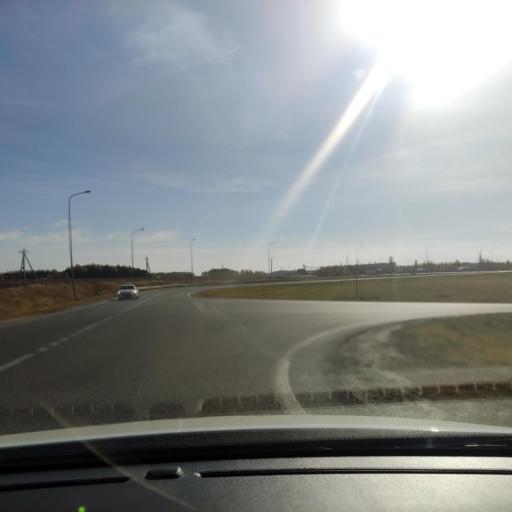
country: RU
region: Tatarstan
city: Vysokaya Gora
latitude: 55.7464
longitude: 49.4009
